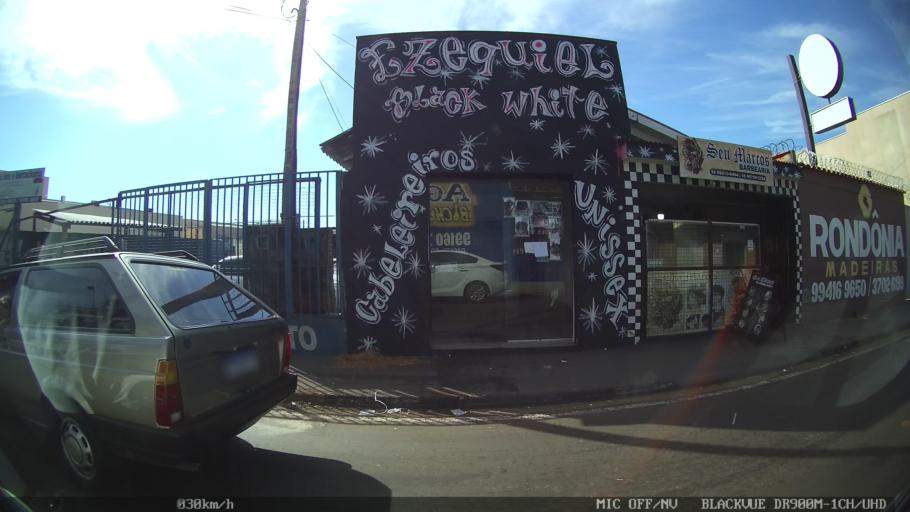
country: BR
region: Sao Paulo
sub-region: Franca
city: Franca
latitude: -20.5296
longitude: -47.4250
